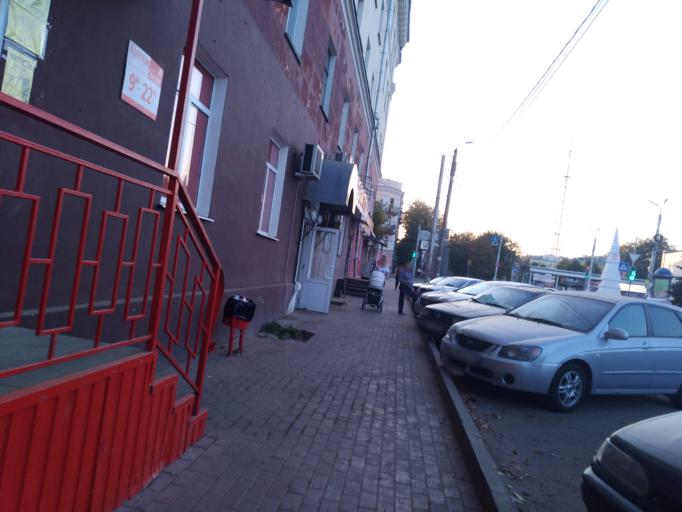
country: RU
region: Kaluga
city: Kaluga
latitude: 54.5193
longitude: 36.2688
